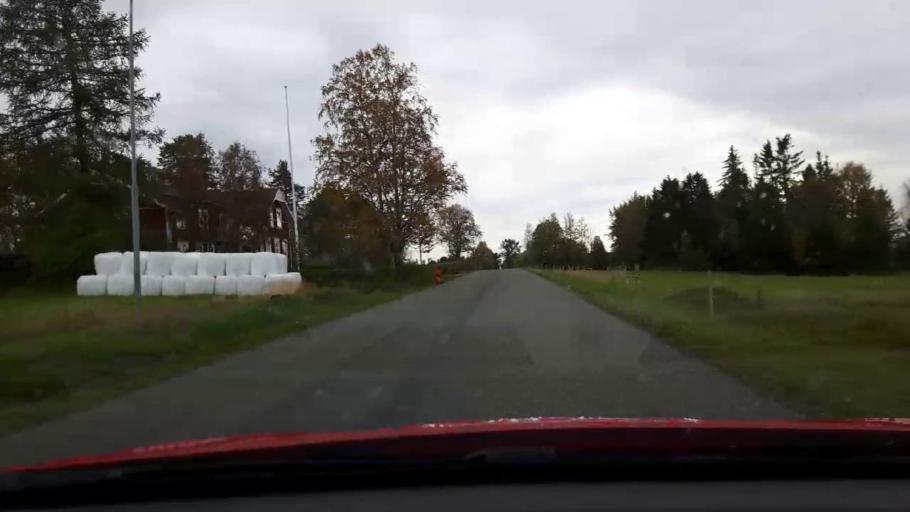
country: SE
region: Jaemtland
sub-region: Bergs Kommun
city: Hoverberg
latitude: 62.9603
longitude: 14.4900
